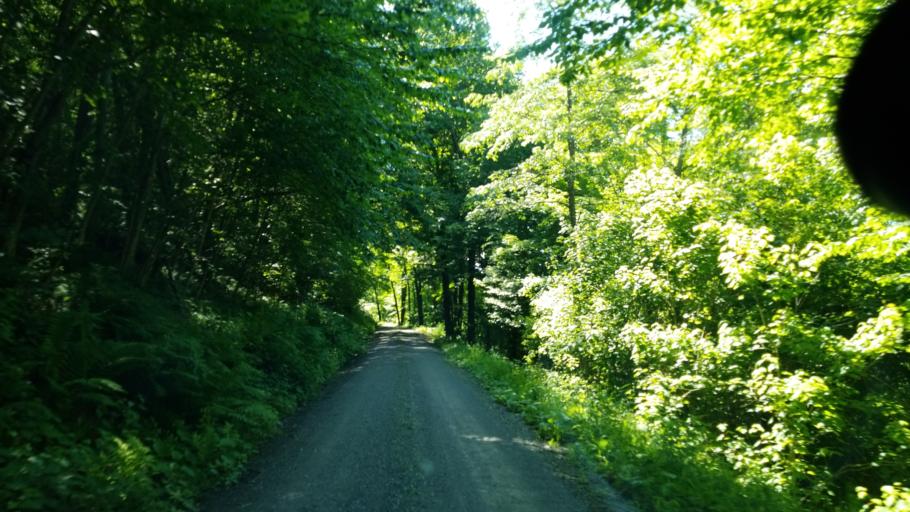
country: US
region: Pennsylvania
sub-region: Clearfield County
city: Clearfield
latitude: 41.2182
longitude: -78.3833
